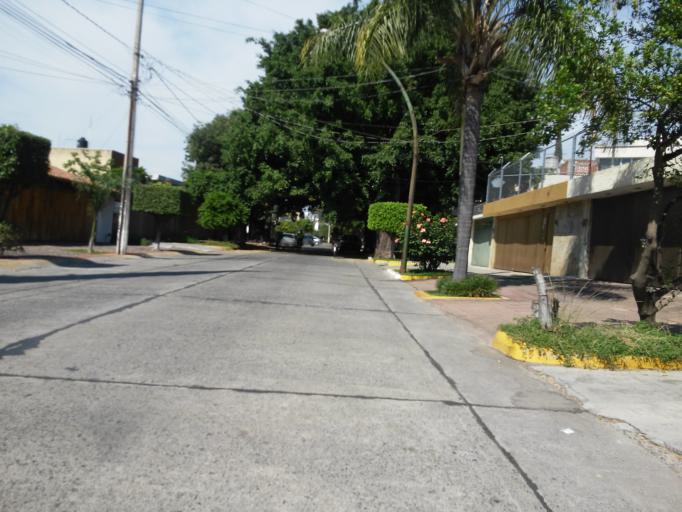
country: MX
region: Jalisco
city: Guadalajara
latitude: 20.6595
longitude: -103.3999
